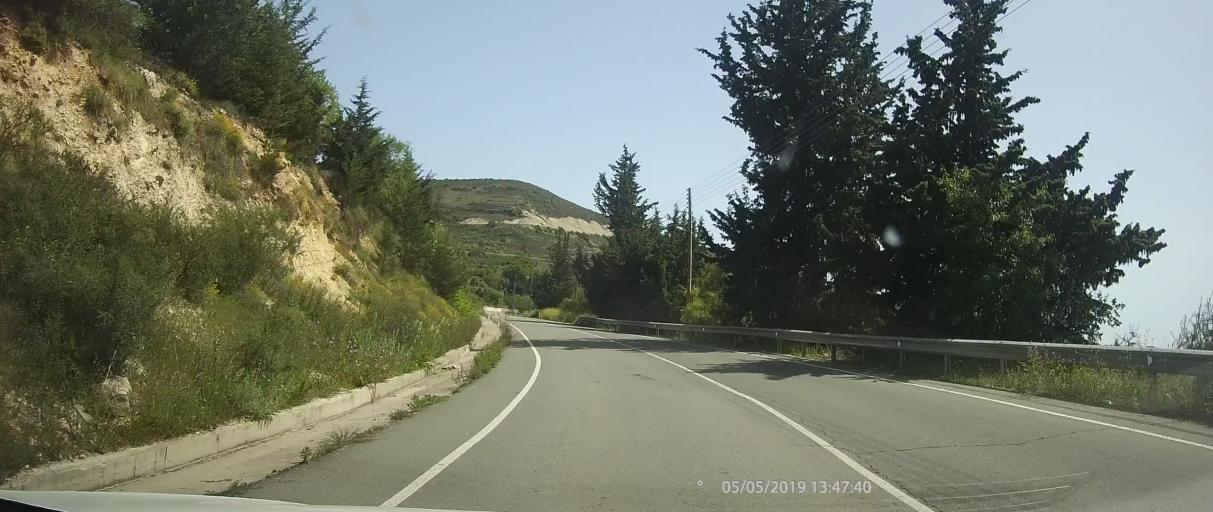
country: CY
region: Limassol
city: Pachna
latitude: 34.8640
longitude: 32.7555
